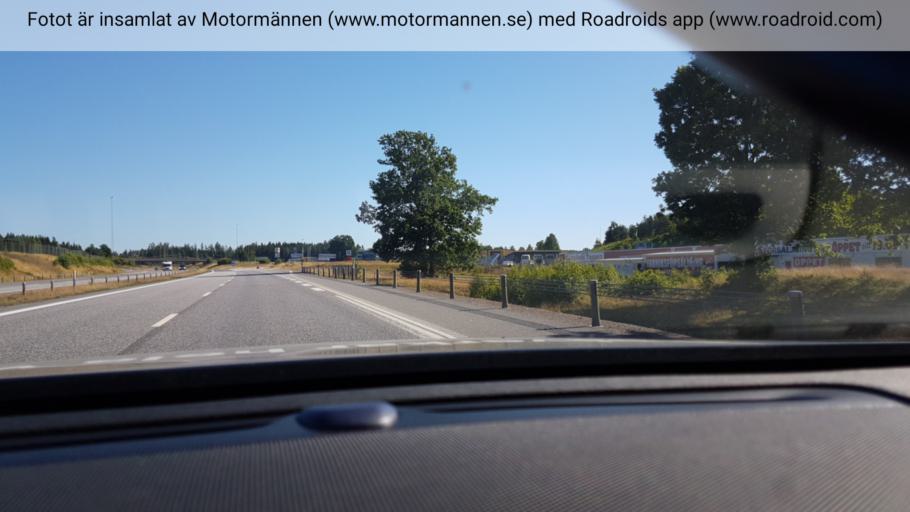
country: SE
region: Kronoberg
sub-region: Markaryds Kommun
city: Stromsnasbruk
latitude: 56.5569
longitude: 13.7184
